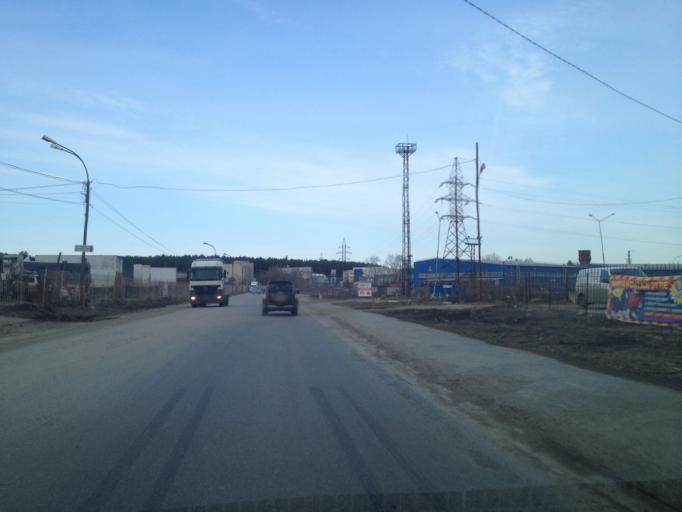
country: RU
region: Sverdlovsk
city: Yekaterinburg
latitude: 56.9098
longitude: 60.6240
